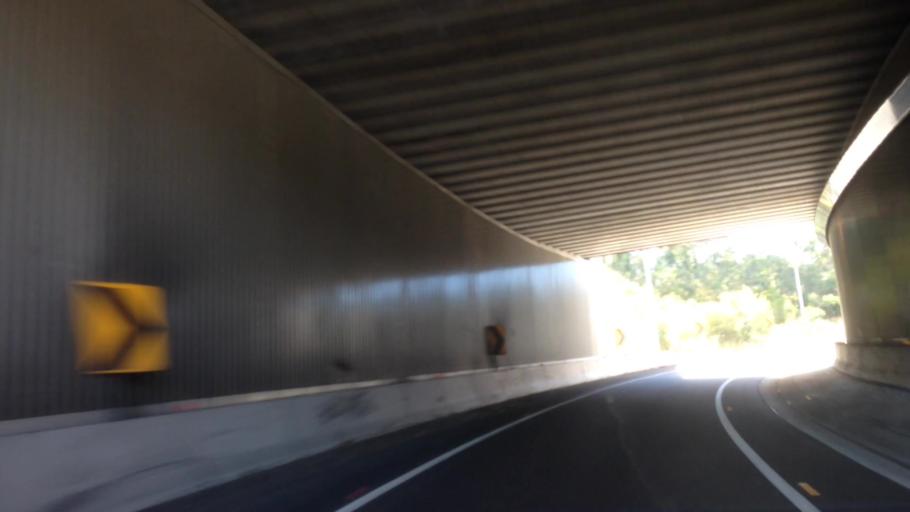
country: AU
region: New South Wales
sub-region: Lake Macquarie Shire
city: Holmesville
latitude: -32.8882
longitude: 151.5991
